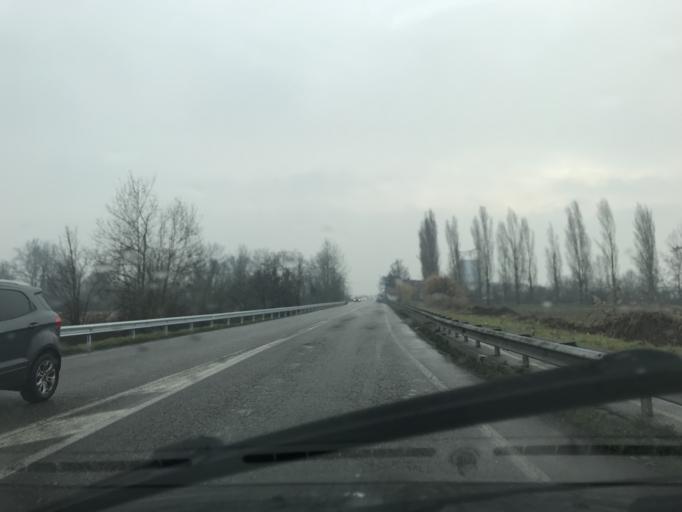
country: IT
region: Lombardy
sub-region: Provincia di Lodi
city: Massalengo-Motta Vigana
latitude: 45.2741
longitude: 9.5031
